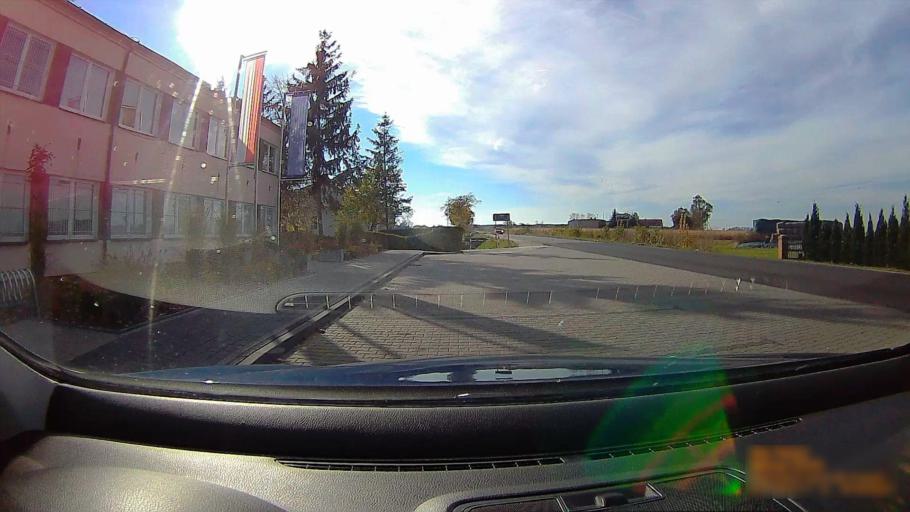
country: PL
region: Greater Poland Voivodeship
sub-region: Powiat ostrzeszowski
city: Doruchow
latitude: 51.4104
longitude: 18.0749
